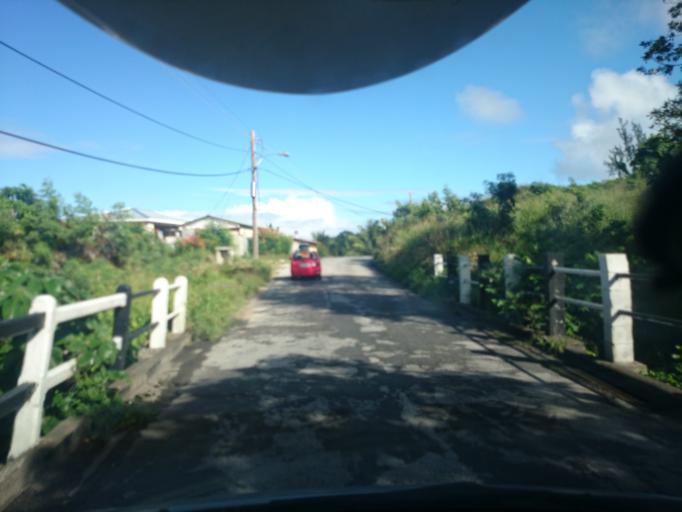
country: BB
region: Saint Joseph
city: Bathsheba
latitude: 13.2081
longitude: -59.5332
